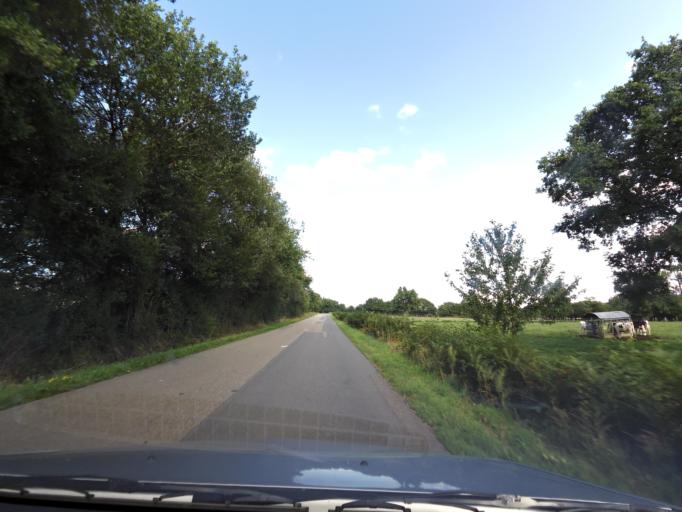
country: FR
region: Brittany
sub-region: Departement d'Ille-et-Vilaine
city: Saint-Senoux
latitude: 47.9155
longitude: -1.8124
